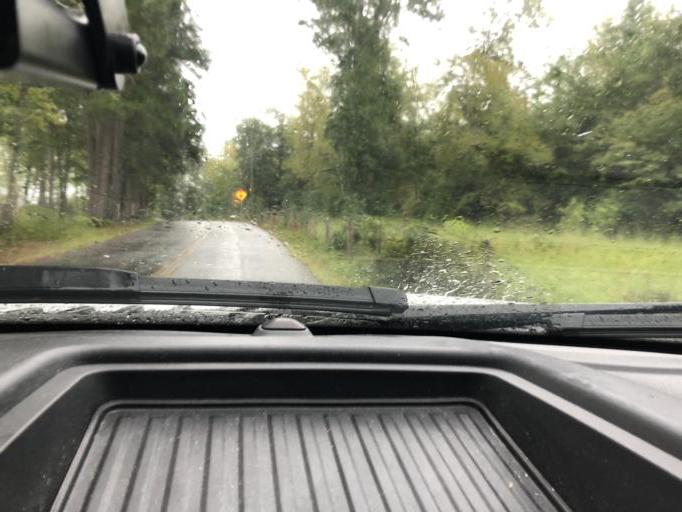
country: US
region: Georgia
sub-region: Putnam County
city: Jefferson
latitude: 33.3904
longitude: -83.2511
